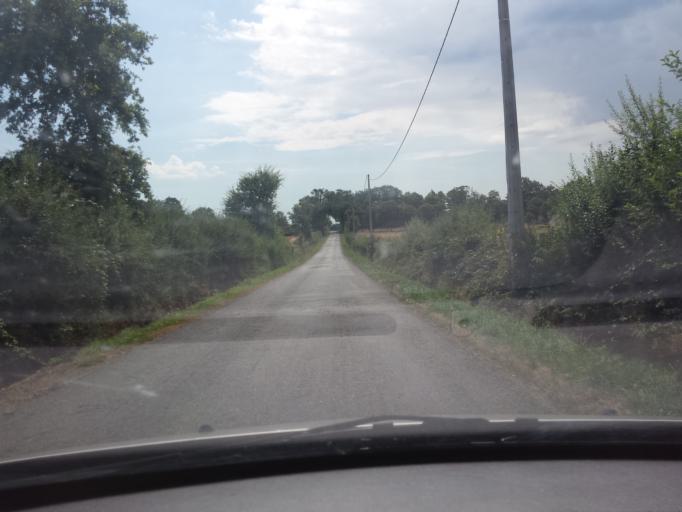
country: FR
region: Poitou-Charentes
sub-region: Departement de la Vienne
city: Availles-Limouzine
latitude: 46.0882
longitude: 0.7310
